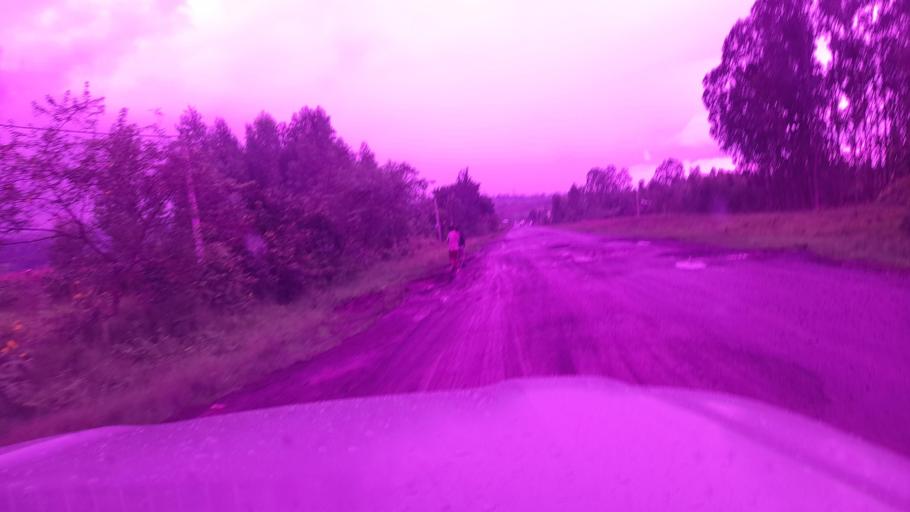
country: ET
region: Oromiya
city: Jima
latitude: 7.7090
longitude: 37.0770
